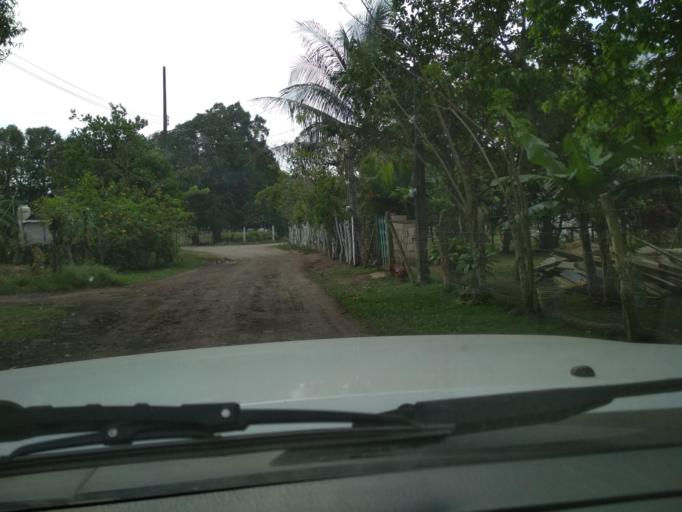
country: MX
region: Veracruz
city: El Tejar
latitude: 19.0730
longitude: -96.1695
